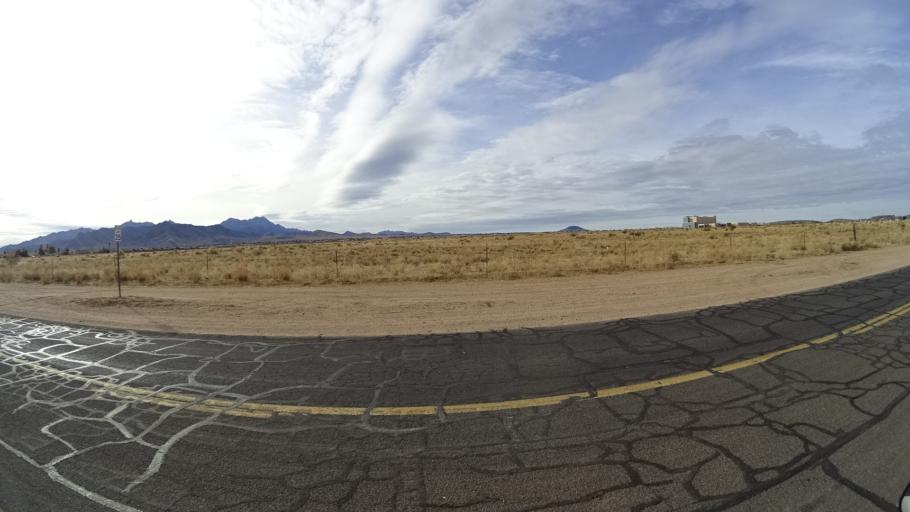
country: US
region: Arizona
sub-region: Mohave County
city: New Kingman-Butler
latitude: 35.2249
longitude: -113.9807
